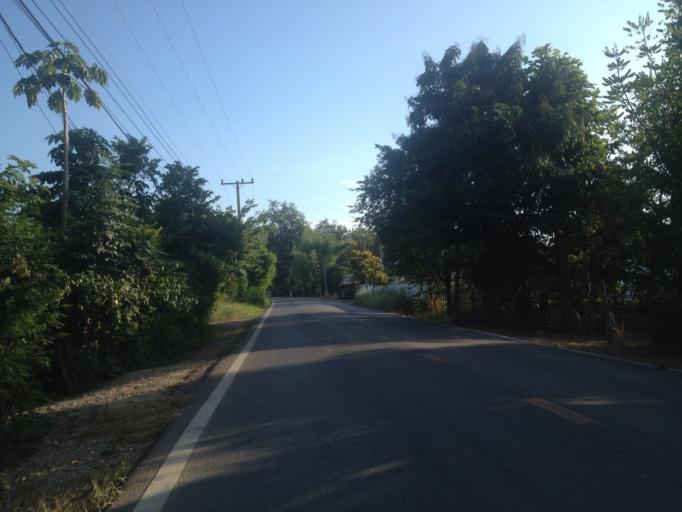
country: TH
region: Chiang Mai
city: San Pa Tong
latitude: 18.5927
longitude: 98.8619
